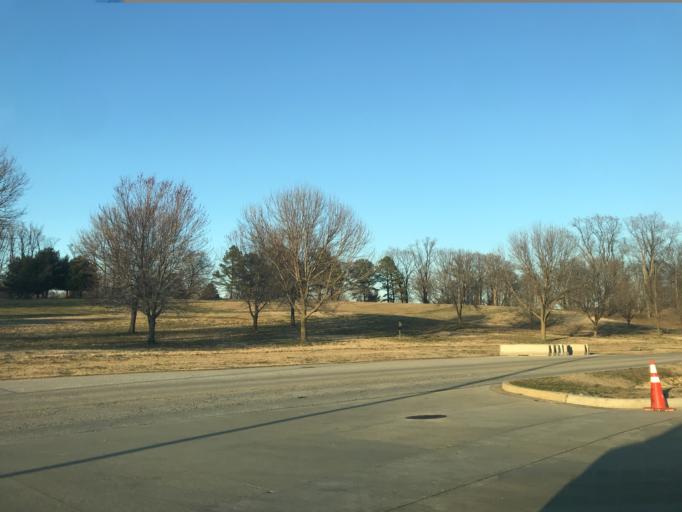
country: US
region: Maryland
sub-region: Anne Arundel County
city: Naval Academy
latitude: 38.9961
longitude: -76.4685
